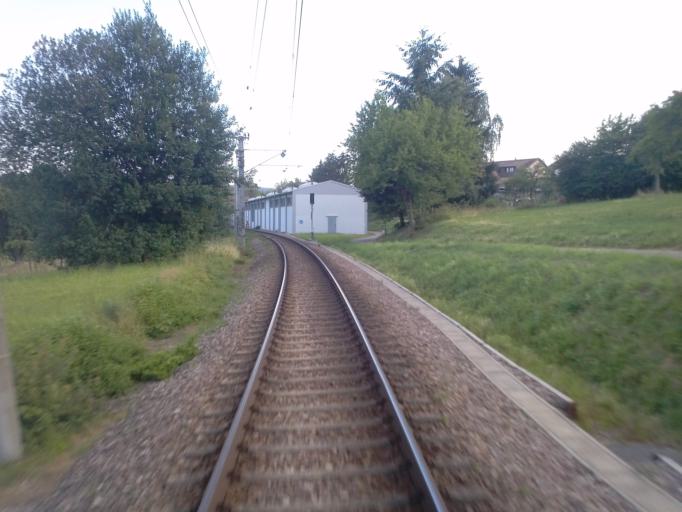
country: DE
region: Baden-Wuerttemberg
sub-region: Karlsruhe Region
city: Dobel
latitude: 48.8716
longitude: 8.5123
